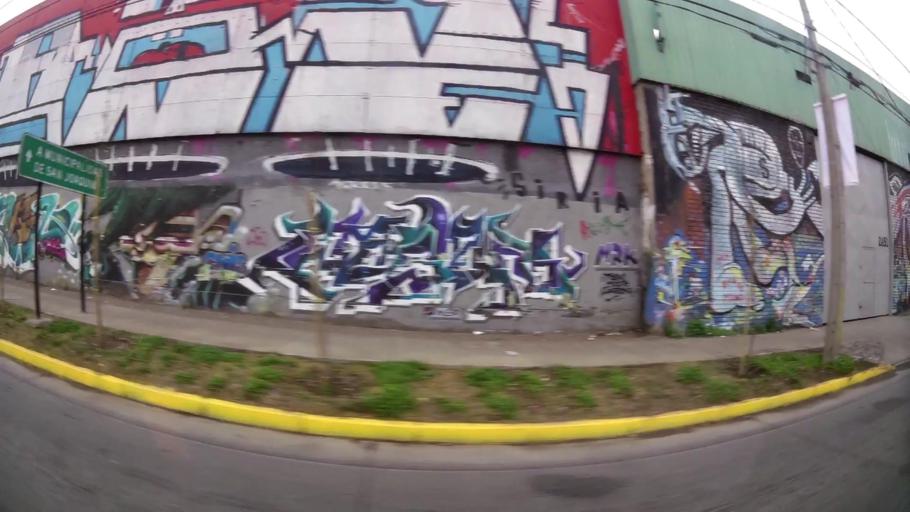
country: CL
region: Santiago Metropolitan
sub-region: Provincia de Santiago
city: Santiago
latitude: -33.4799
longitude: -70.6420
